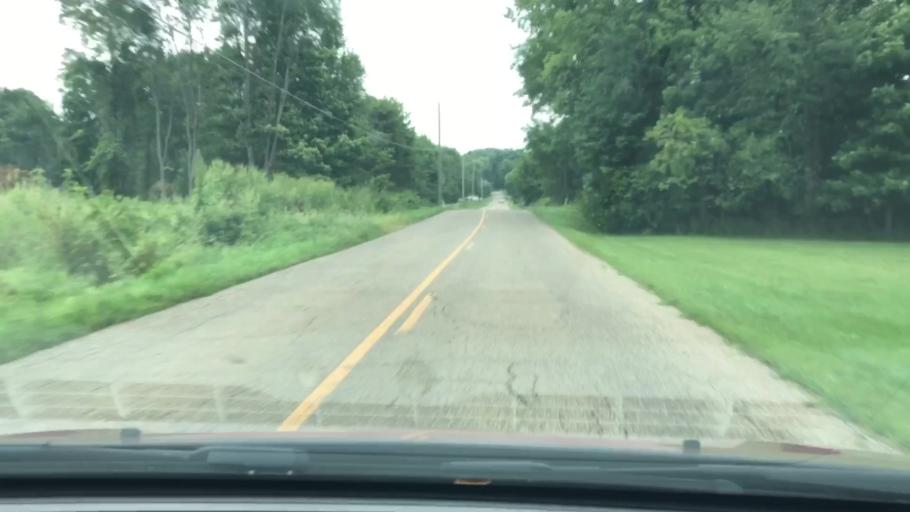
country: US
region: Ohio
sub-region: Knox County
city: Centerburg
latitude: 40.3166
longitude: -82.7260
